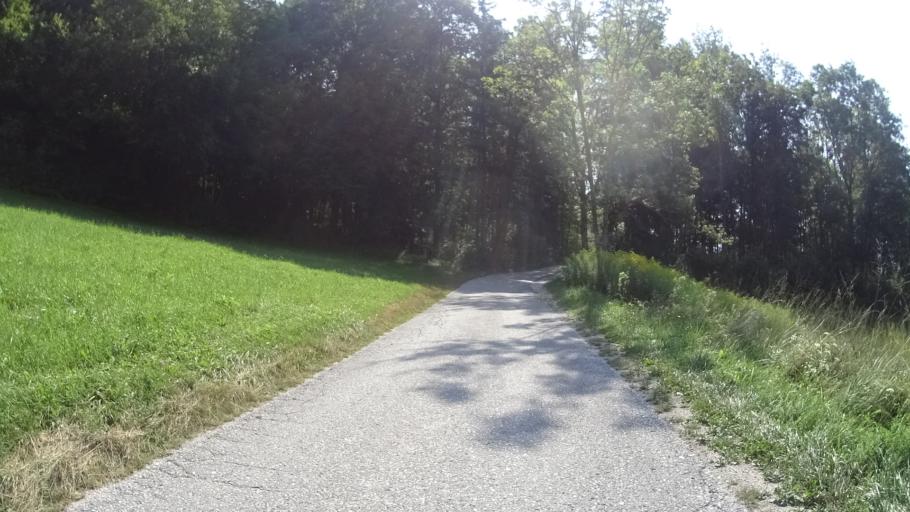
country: AT
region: Carinthia
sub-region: Politischer Bezirk Volkermarkt
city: Gallizien
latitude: 46.5699
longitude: 14.5256
